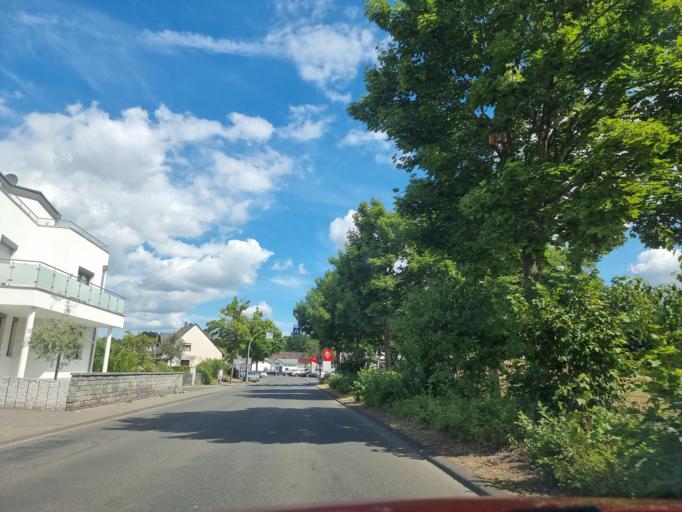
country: DE
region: Rheinland-Pfalz
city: Wittlich
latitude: 49.9792
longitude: 6.8924
